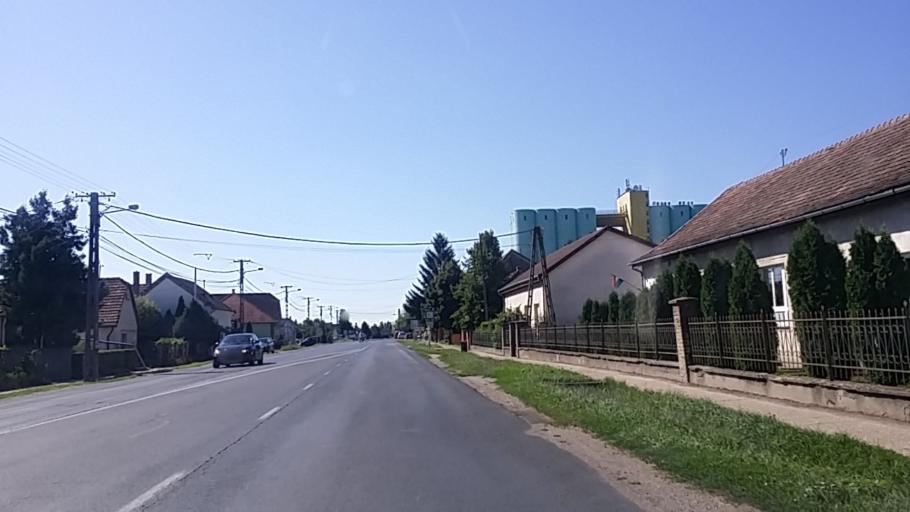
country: HU
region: Fejer
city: Sarbogard
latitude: 46.8581
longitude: 18.6311
